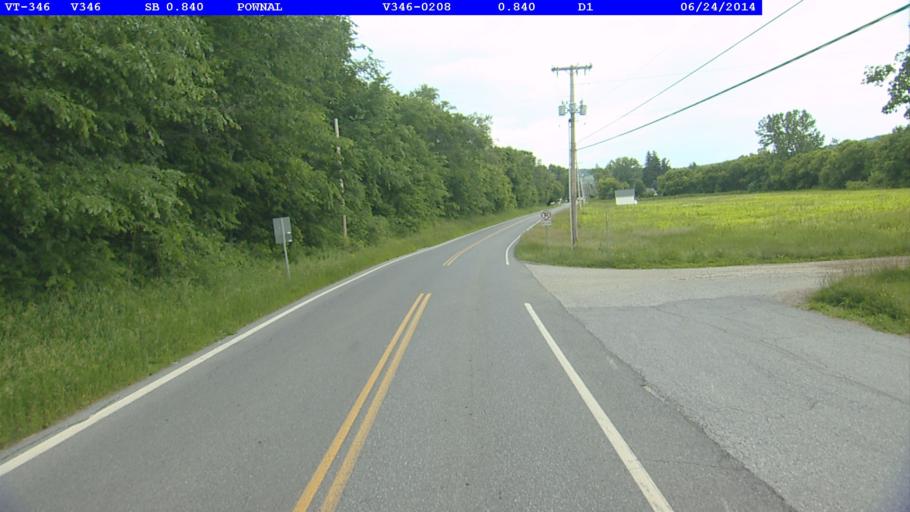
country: US
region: Massachusetts
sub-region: Berkshire County
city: Williamstown
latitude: 42.7728
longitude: -73.2408
